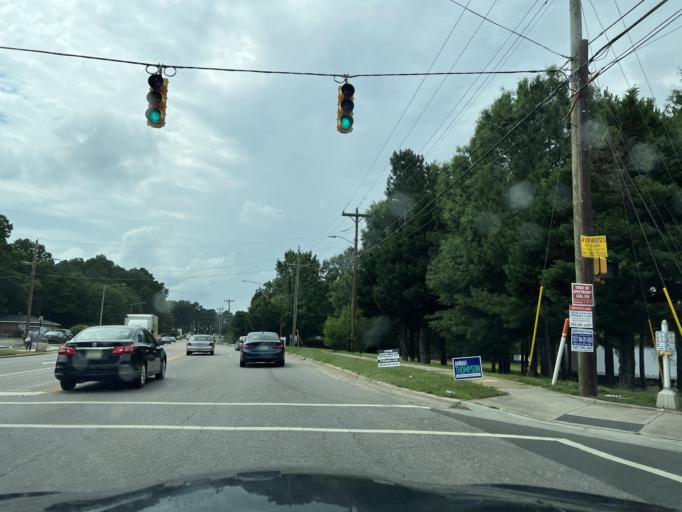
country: US
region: North Carolina
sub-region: Durham County
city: Durham
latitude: 36.0358
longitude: -78.8935
